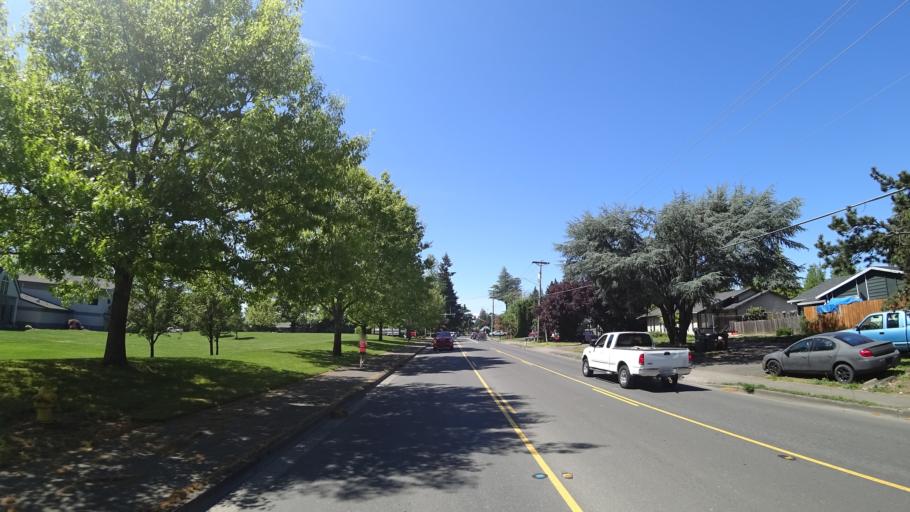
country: US
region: Oregon
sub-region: Washington County
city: Hillsboro
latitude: 45.5039
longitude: -122.9618
